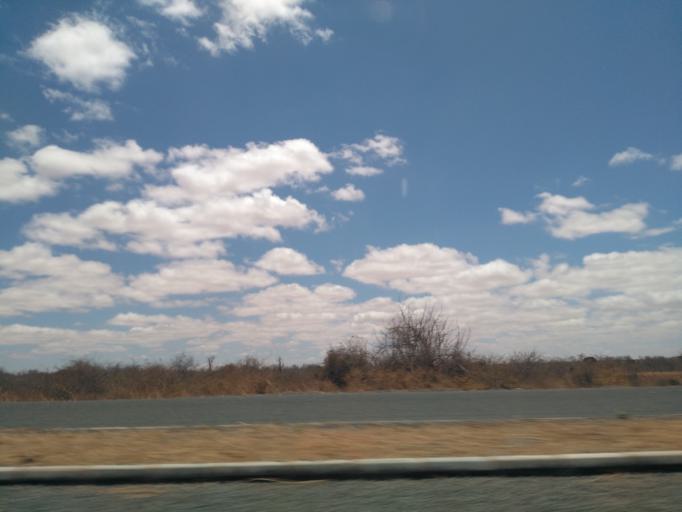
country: TZ
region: Dodoma
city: Kisasa
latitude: -6.1691
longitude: 35.8432
